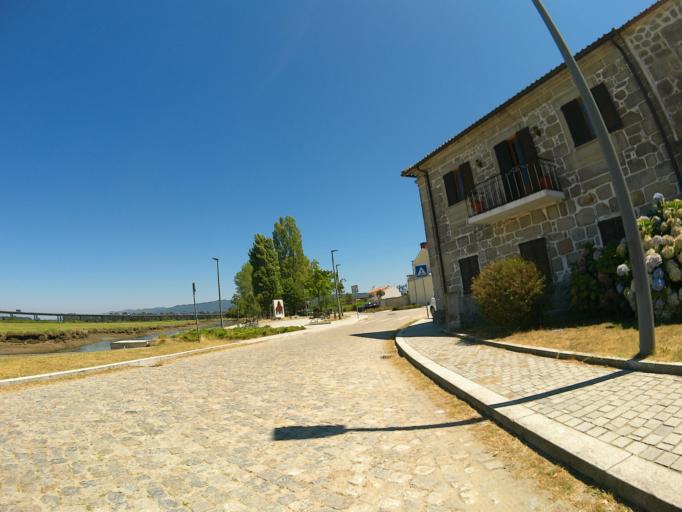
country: PT
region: Viana do Castelo
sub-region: Viana do Castelo
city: Meadela
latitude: 41.6880
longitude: -8.7903
